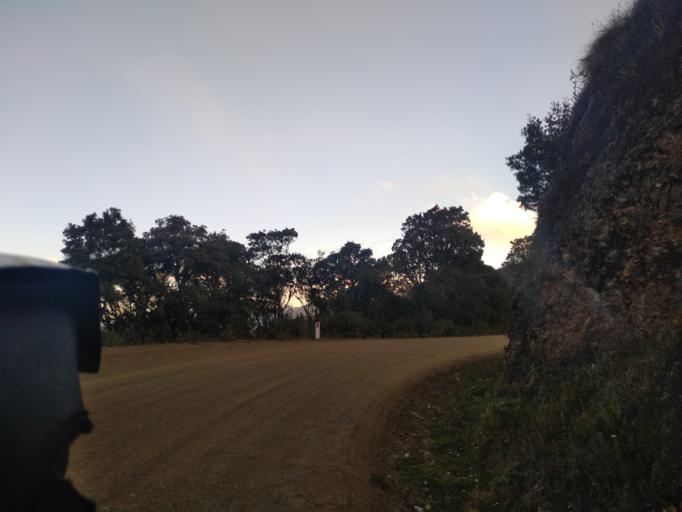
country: PE
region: Amazonas
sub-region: Provincia de Chachapoyas
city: Montevideo
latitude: -6.7160
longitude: -77.8732
